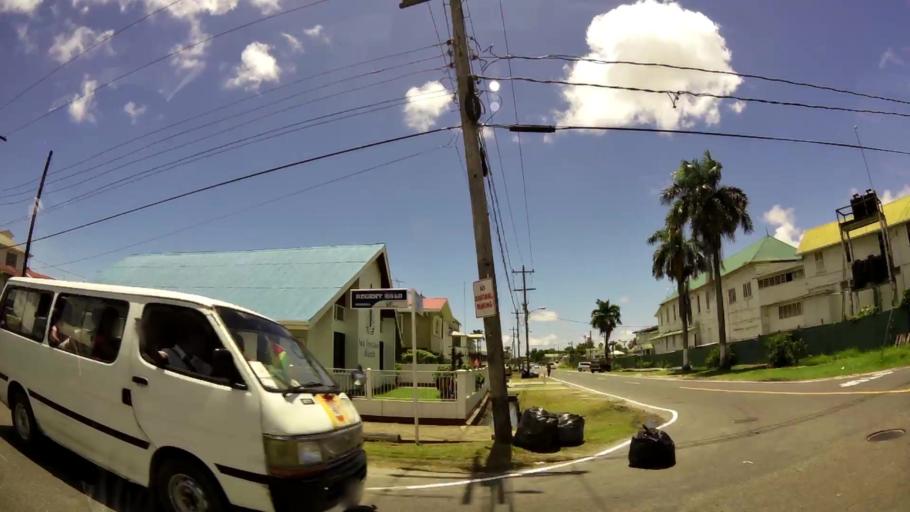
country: GY
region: Demerara-Mahaica
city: Georgetown
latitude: 6.8076
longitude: -58.1510
